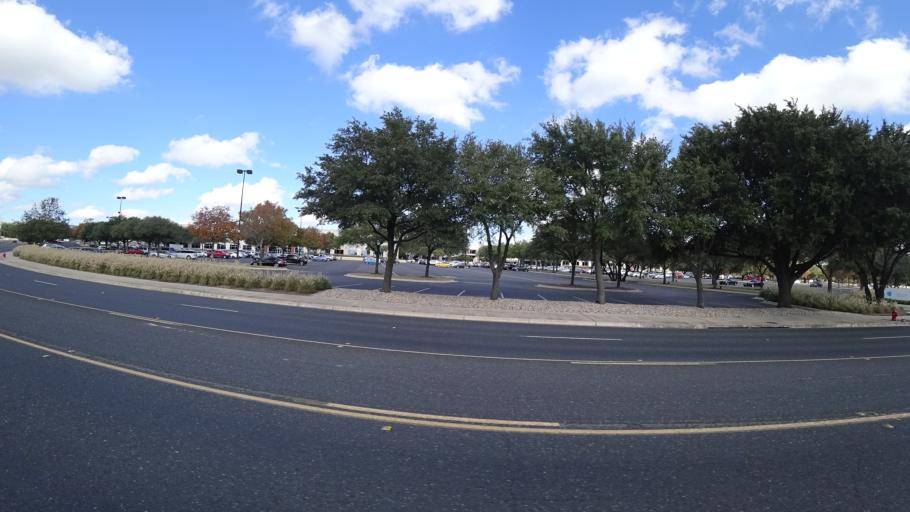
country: US
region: Texas
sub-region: Williamson County
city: Jollyville
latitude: 30.4304
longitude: -97.7362
